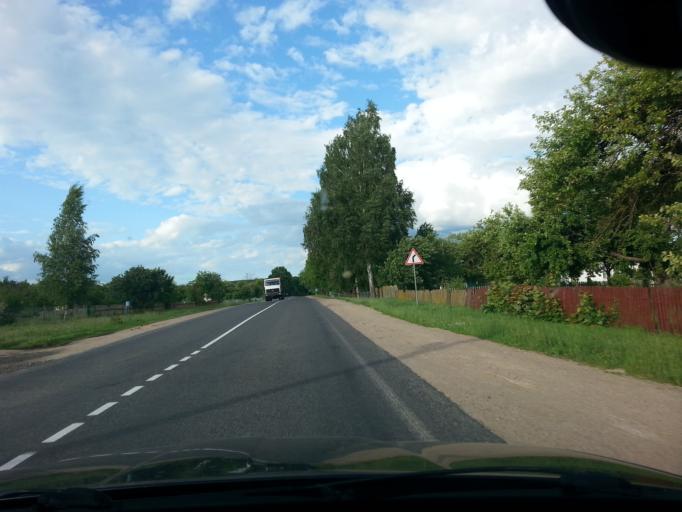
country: BY
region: Grodnenskaya
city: Astravyets
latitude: 54.7768
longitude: 26.0328
